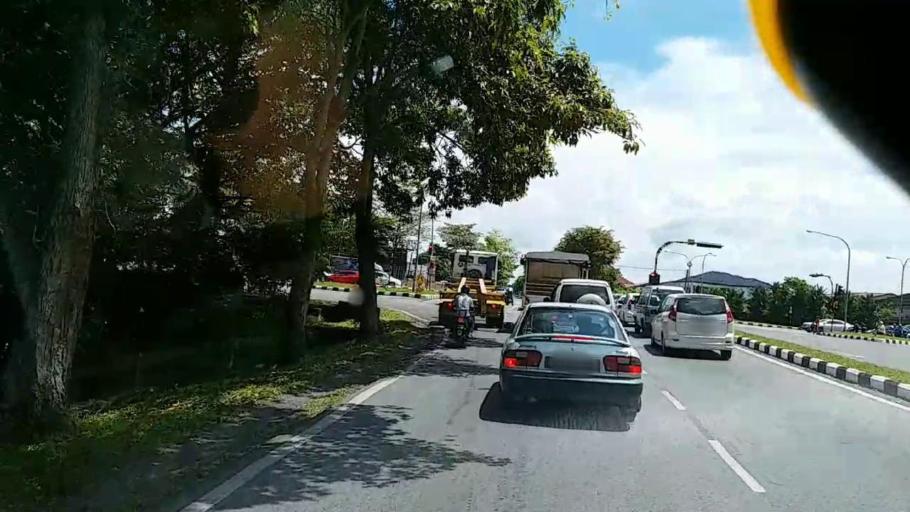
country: MY
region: Sarawak
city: Sibu
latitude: 2.3037
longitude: 111.8335
